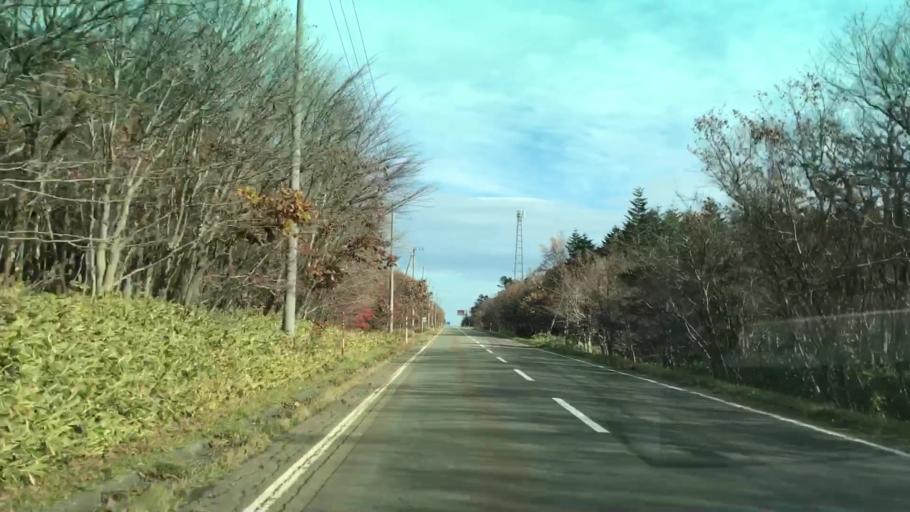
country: JP
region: Hokkaido
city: Obihiro
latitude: 42.0340
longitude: 143.2817
